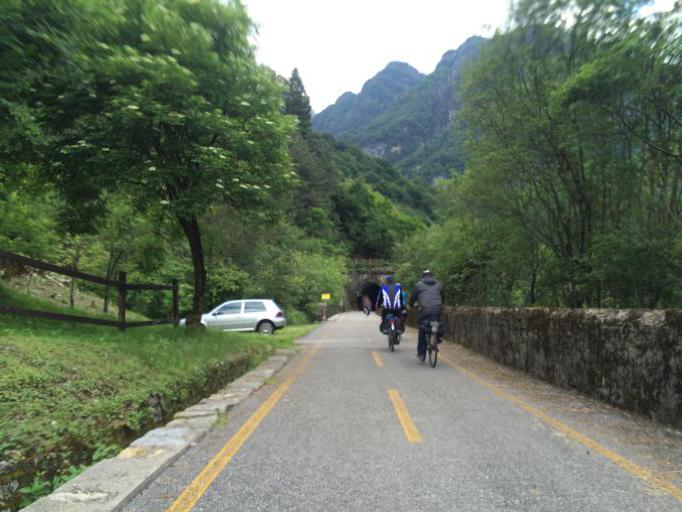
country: IT
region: Friuli Venezia Giulia
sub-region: Provincia di Udine
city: Dogna
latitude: 46.4539
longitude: 13.3152
